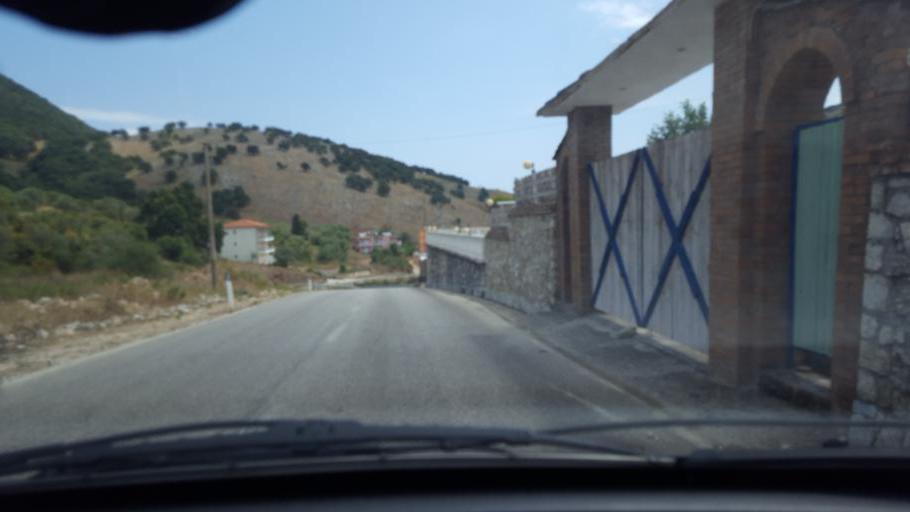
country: AL
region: Vlore
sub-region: Rrethi i Vlores
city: Himare
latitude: 40.0895
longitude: 19.7655
